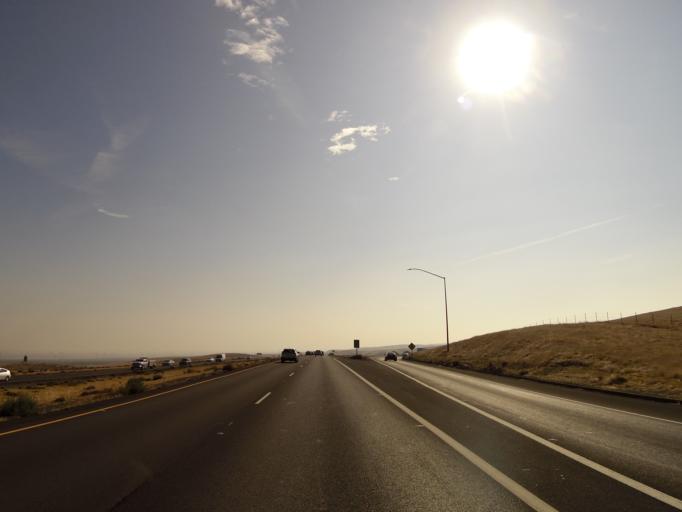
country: US
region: California
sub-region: Kings County
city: Kettleman City
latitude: 35.9840
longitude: -119.9630
